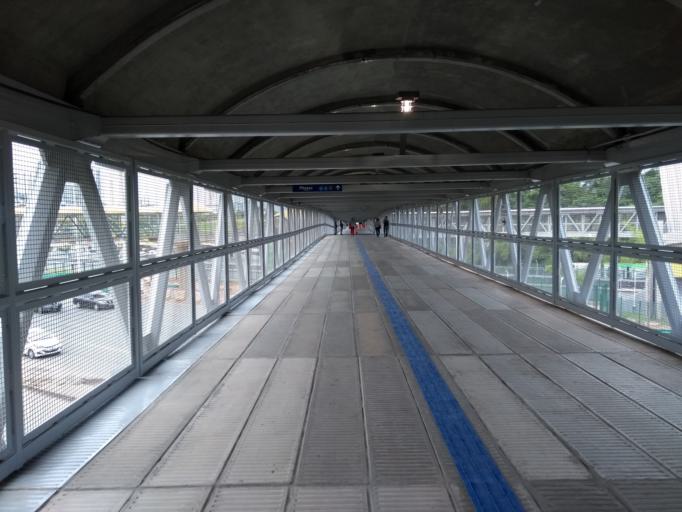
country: BR
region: Bahia
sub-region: Salvador
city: Salvador
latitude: -12.9446
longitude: -38.4215
